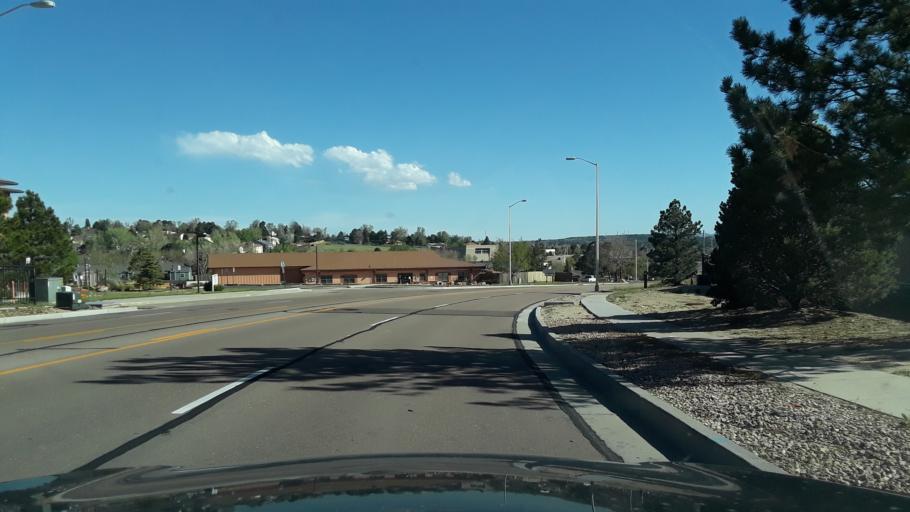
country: US
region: Colorado
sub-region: El Paso County
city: Air Force Academy
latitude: 38.9517
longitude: -104.7916
